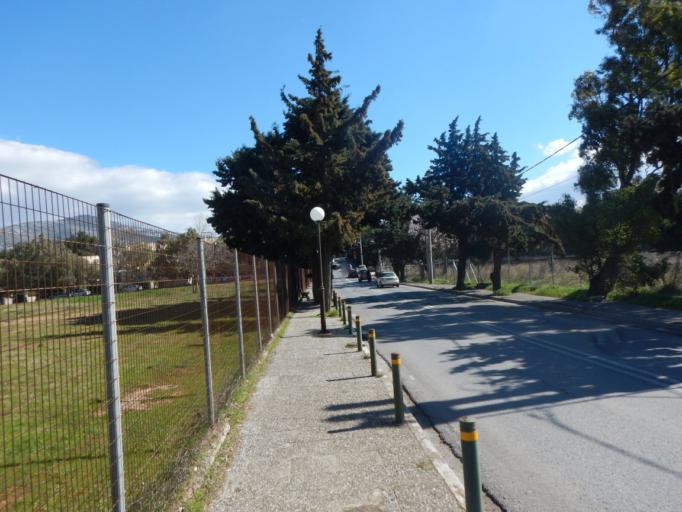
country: GR
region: Attica
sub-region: Nomarchia Athinas
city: Kifisia
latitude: 38.0666
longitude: 23.8233
